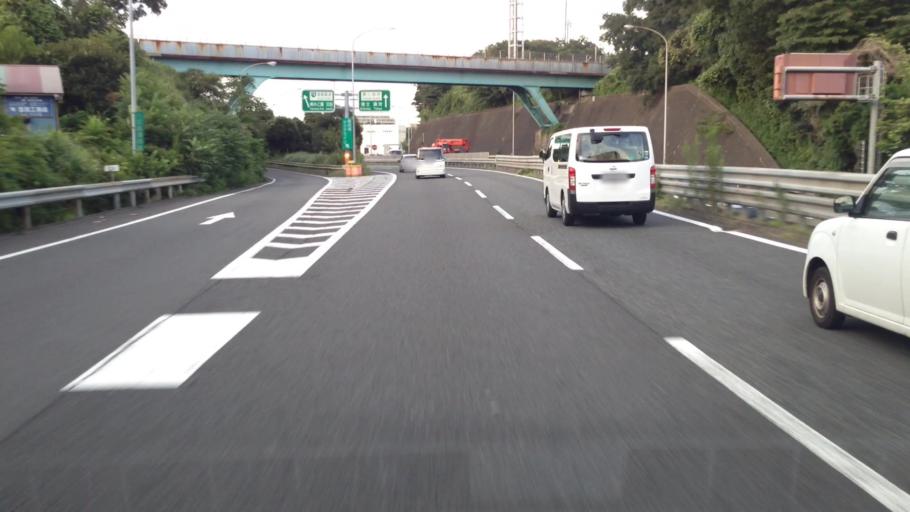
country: JP
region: Kanagawa
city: Yokohama
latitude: 35.4740
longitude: 139.5957
